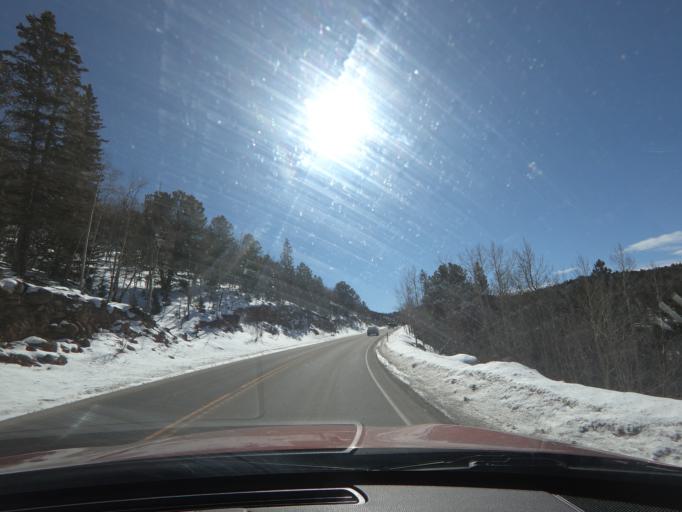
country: US
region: Colorado
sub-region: Teller County
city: Cripple Creek
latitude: 38.8094
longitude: -105.1249
